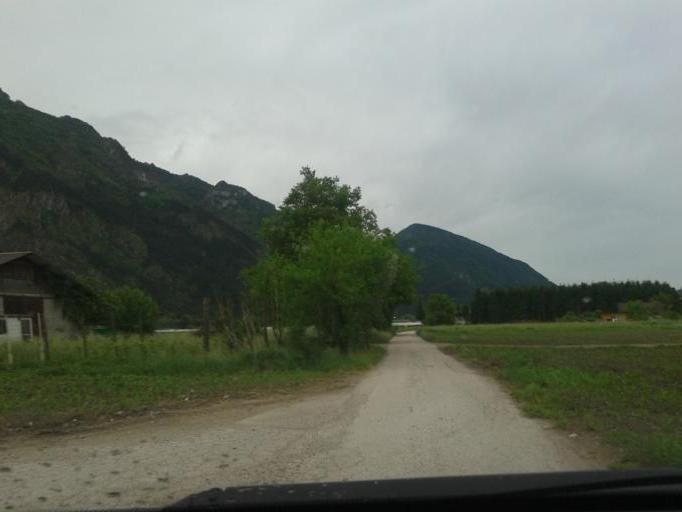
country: IT
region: Trentino-Alto Adige
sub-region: Provincia di Trento
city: Lodrone-Darzo
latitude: 45.8366
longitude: 10.5552
